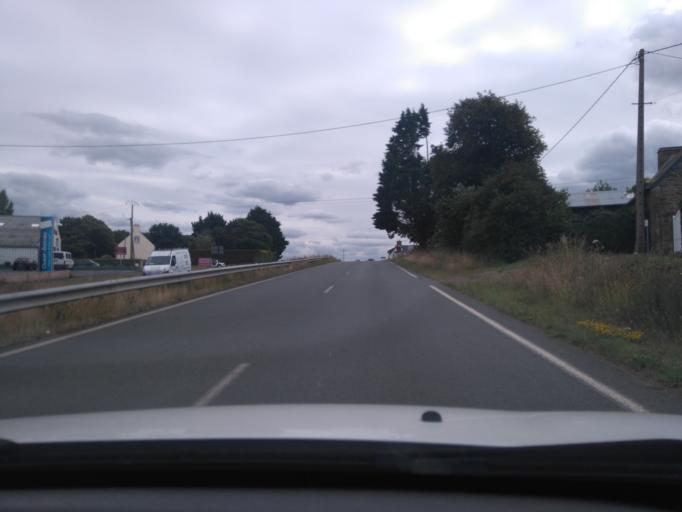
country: FR
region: Brittany
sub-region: Departement des Cotes-d'Armor
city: Saint-Quay-Perros
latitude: 48.7809
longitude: -3.4492
